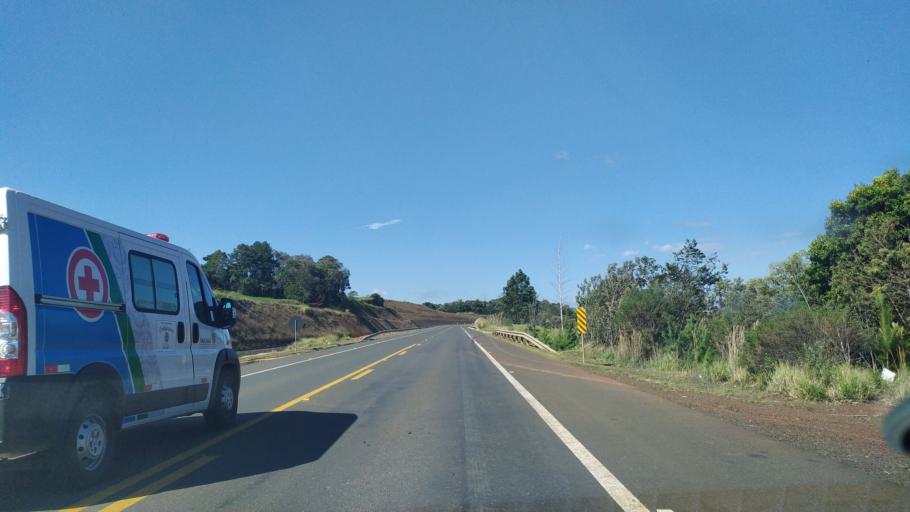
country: BR
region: Parana
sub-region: Ortigueira
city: Ortigueira
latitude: -24.2677
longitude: -50.8083
